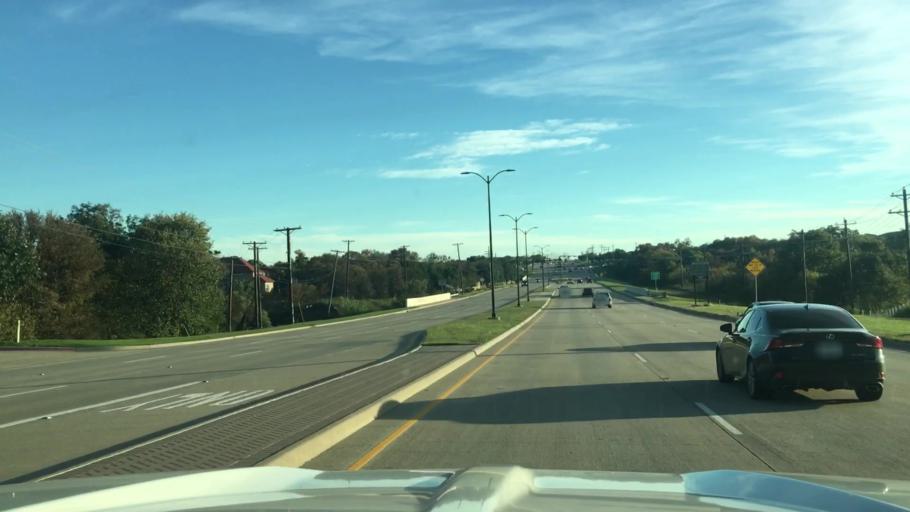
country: US
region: Texas
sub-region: Collin County
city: Frisco
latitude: 33.1801
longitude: -96.8030
